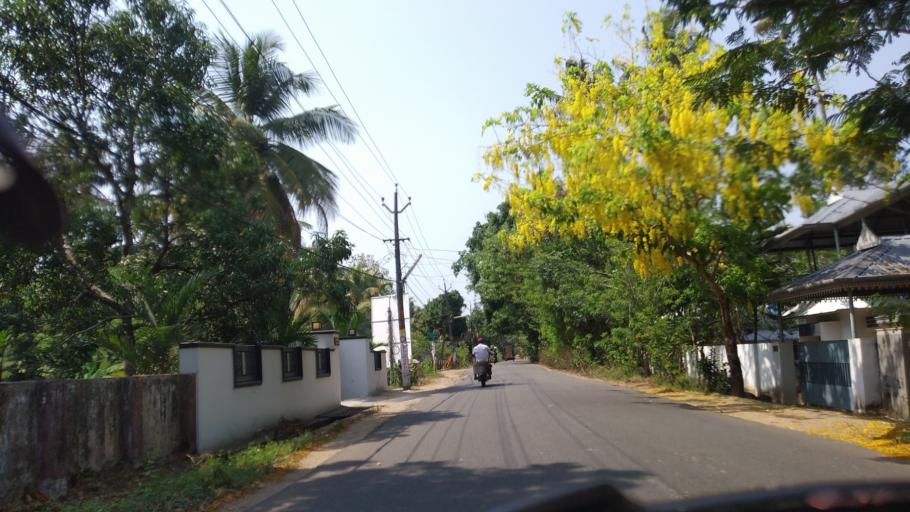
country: IN
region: Kerala
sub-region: Thrissur District
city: Kodungallur
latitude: 10.2437
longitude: 76.1502
